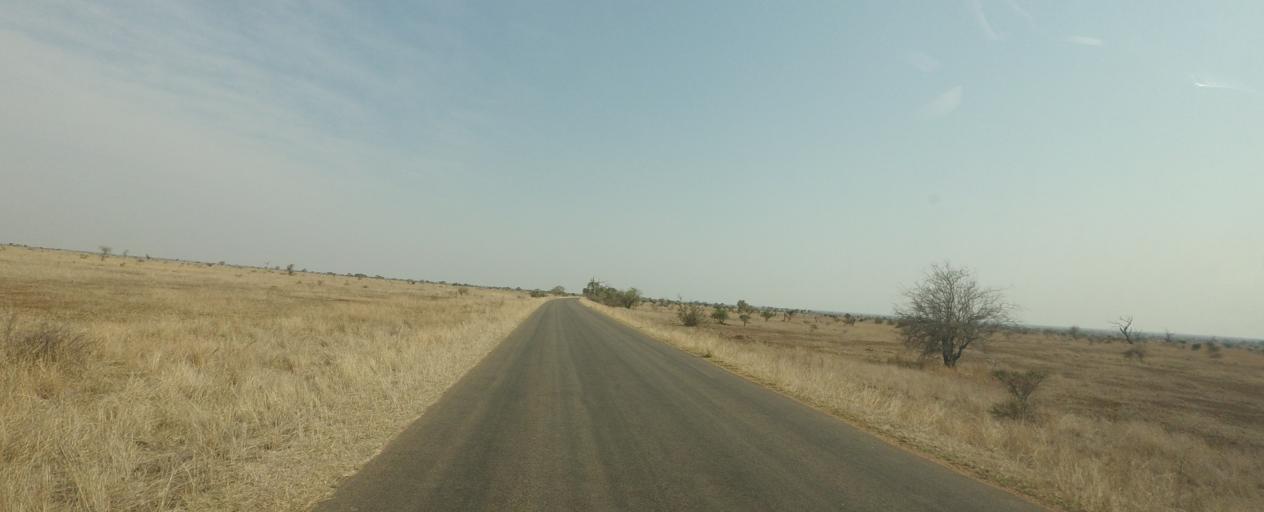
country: ZA
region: Limpopo
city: Thulamahashi
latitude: -24.3241
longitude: 31.7527
